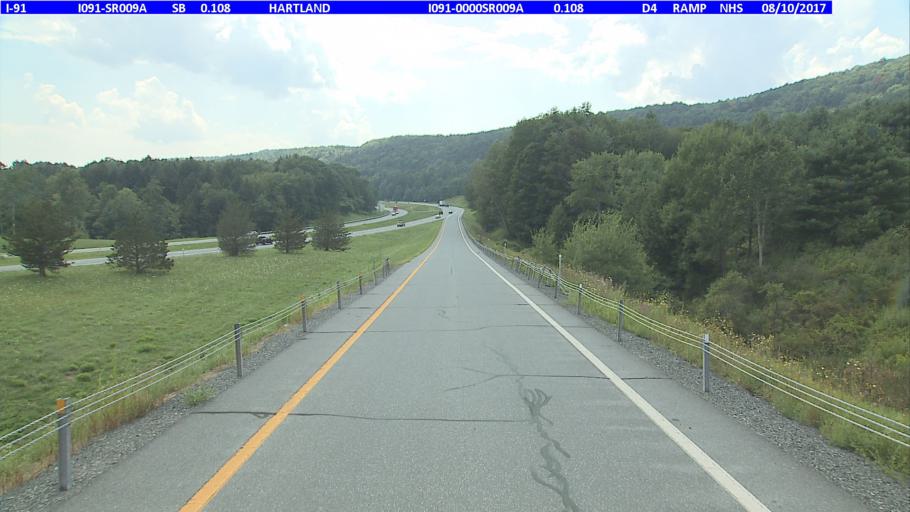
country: US
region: Vermont
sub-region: Windsor County
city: Windsor
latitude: 43.5272
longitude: -72.4039
